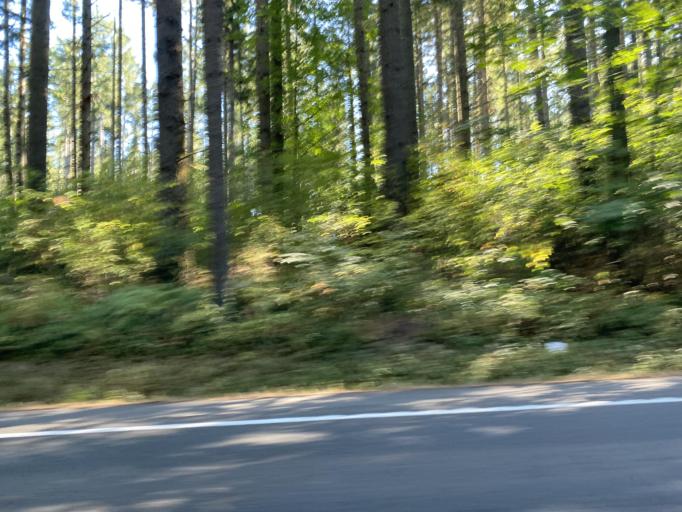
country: US
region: Washington
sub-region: Thurston County
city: Rainier
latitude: 46.9266
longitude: -122.7513
